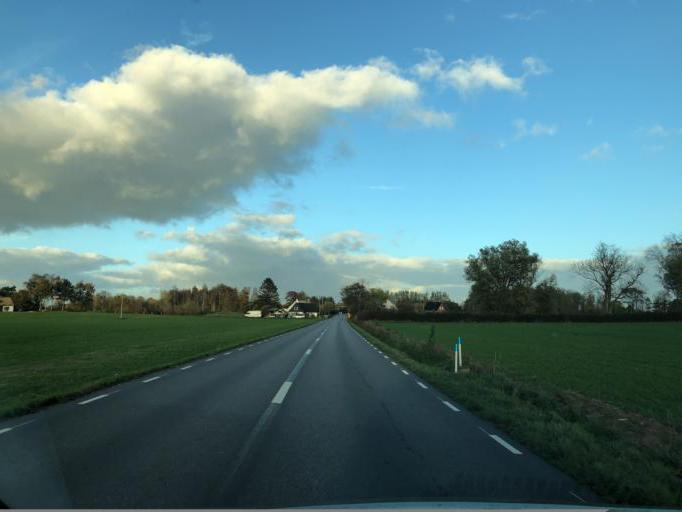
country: SE
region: Skane
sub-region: Svalovs Kommun
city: Teckomatorp
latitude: 55.8439
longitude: 13.1064
